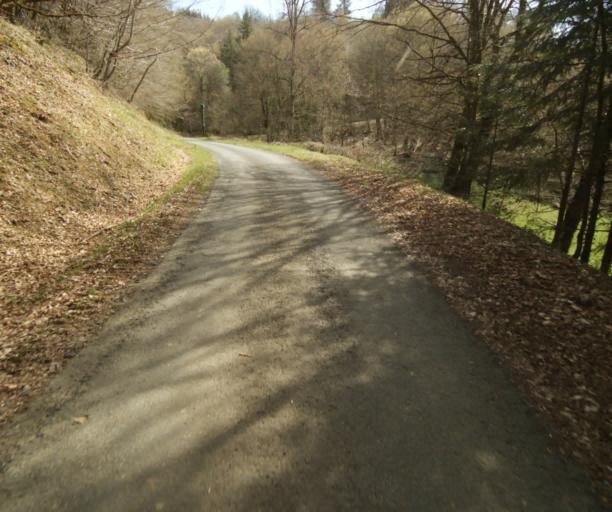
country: FR
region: Limousin
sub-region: Departement de la Correze
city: Naves
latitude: 45.3697
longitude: 1.7880
